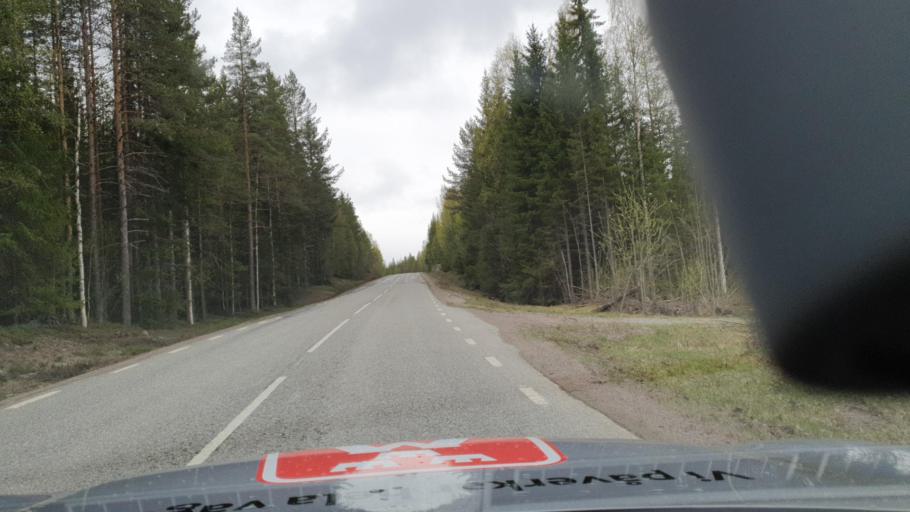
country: SE
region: Vaesterbotten
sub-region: Asele Kommun
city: Asele
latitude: 63.6719
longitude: 17.2559
